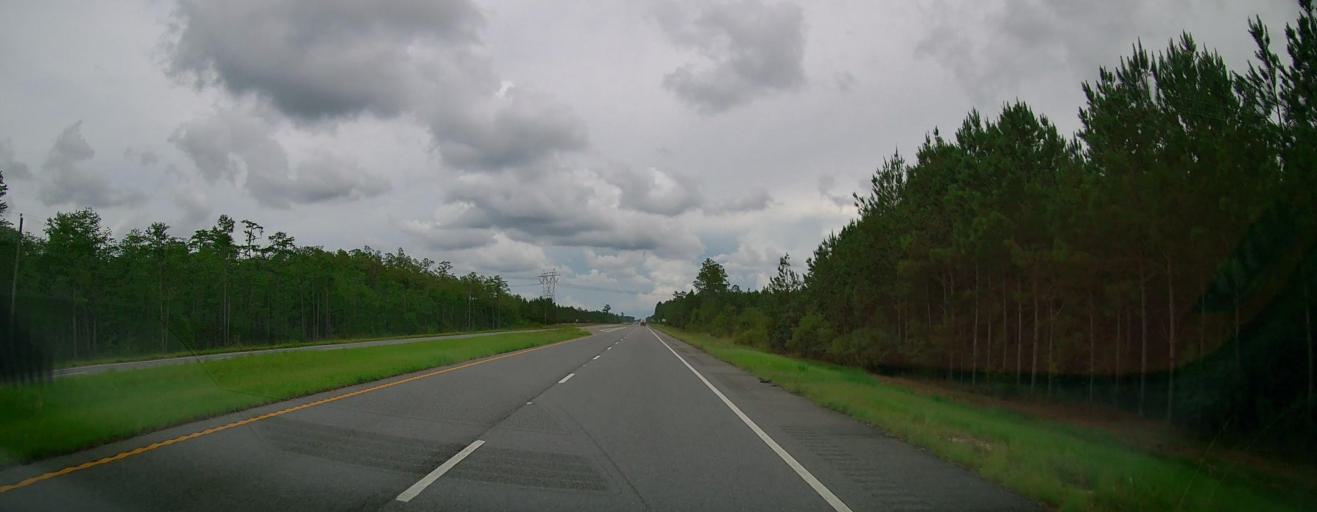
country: US
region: Georgia
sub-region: Wayne County
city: Jesup
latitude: 31.6803
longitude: -82.0901
